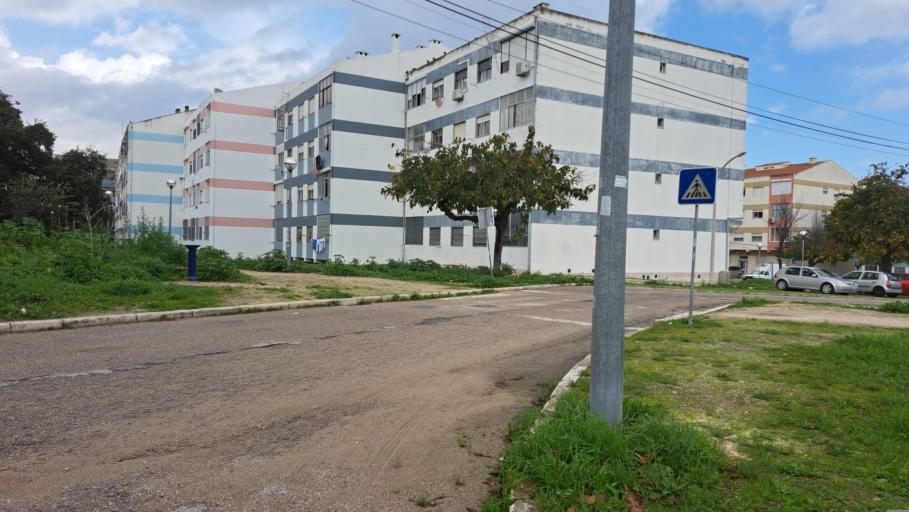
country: PT
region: Setubal
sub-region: Moita
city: Alhos Vedros
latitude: 38.6480
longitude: -9.0430
